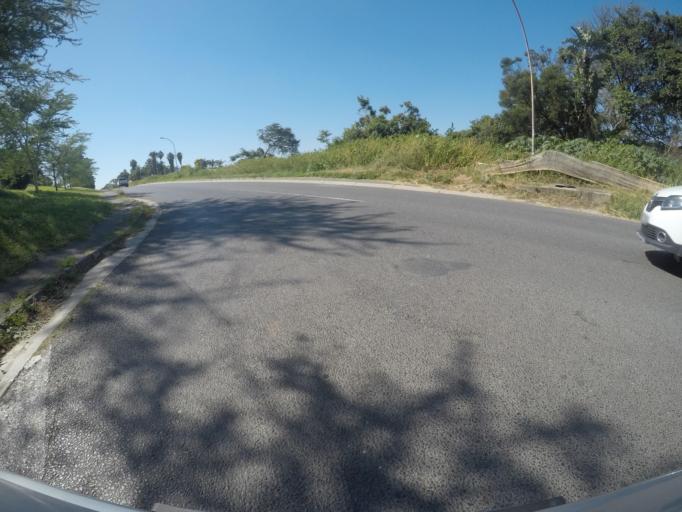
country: ZA
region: Eastern Cape
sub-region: Buffalo City Metropolitan Municipality
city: East London
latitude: -32.9571
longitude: 27.9113
